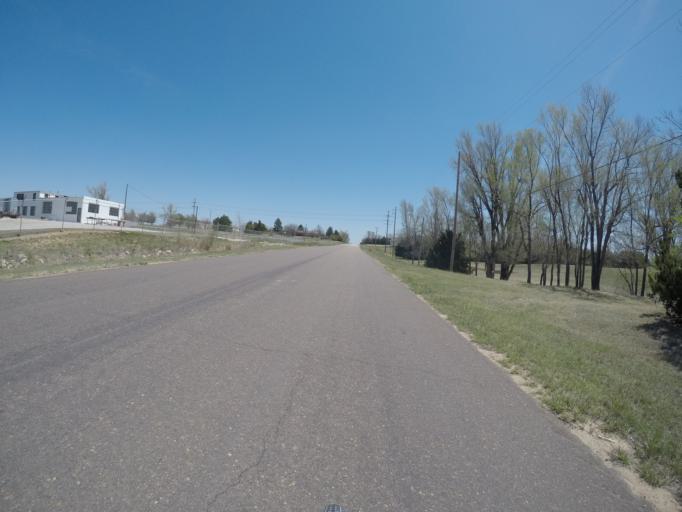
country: US
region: Kansas
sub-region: Pratt County
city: Pratt
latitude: 37.6420
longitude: -98.7589
